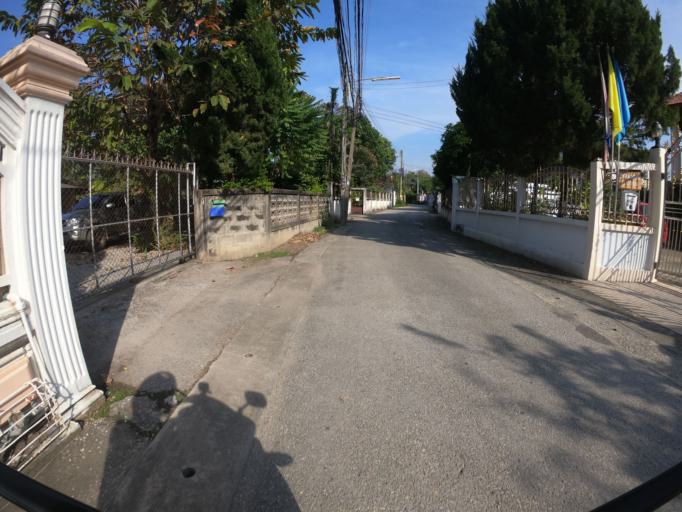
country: TH
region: Chiang Mai
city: Chiang Mai
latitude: 18.8383
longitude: 98.9860
